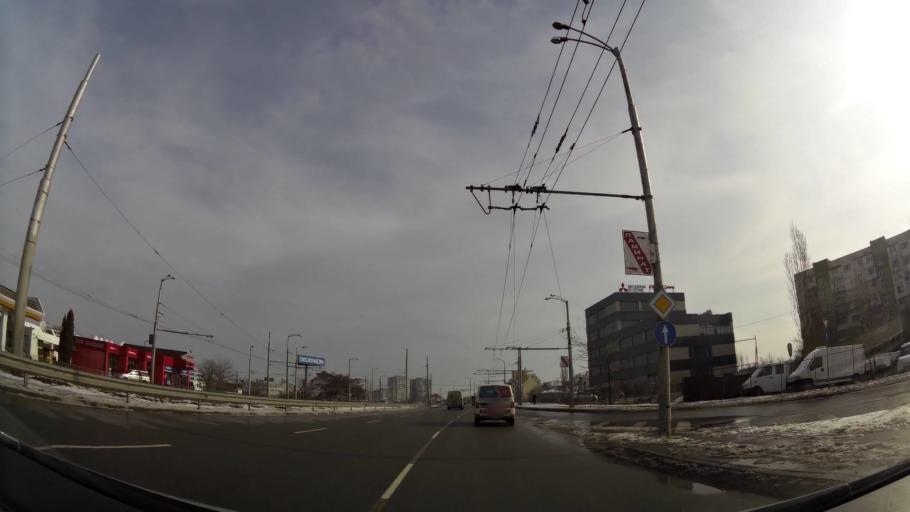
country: BG
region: Sofia-Capital
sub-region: Stolichna Obshtina
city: Sofia
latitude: 42.7088
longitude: 23.3680
